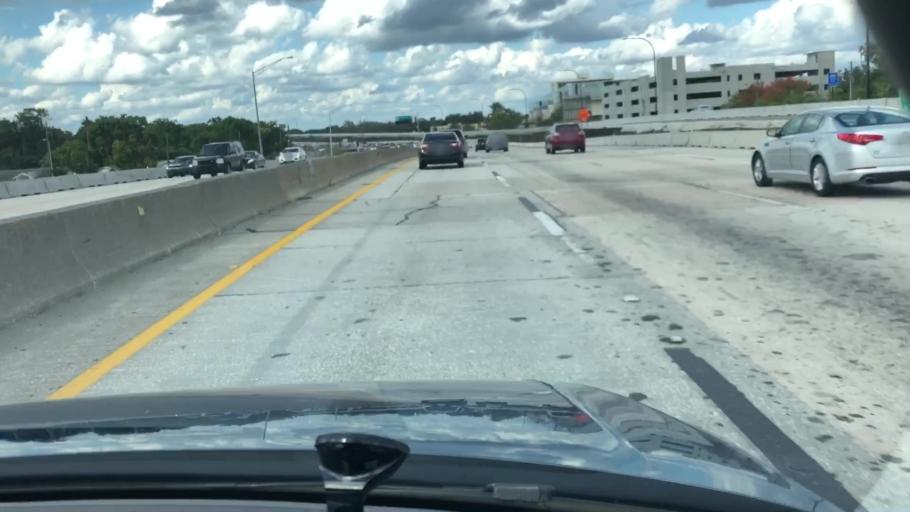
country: US
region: Florida
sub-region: Orange County
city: Fairview Shores
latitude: 28.5824
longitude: -81.3751
